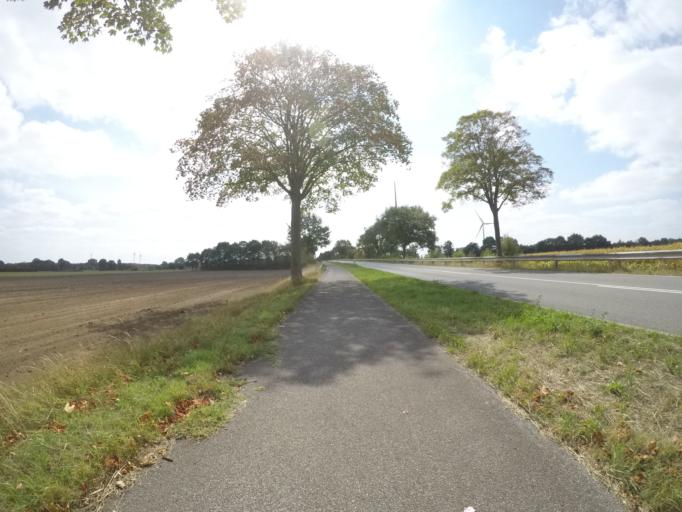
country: DE
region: North Rhine-Westphalia
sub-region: Regierungsbezirk Munster
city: Isselburg
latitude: 51.8081
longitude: 6.4772
